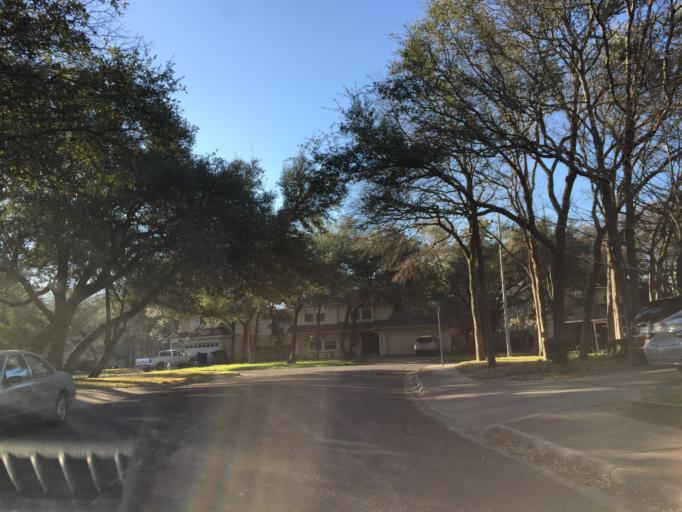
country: US
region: Texas
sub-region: Williamson County
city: Jollyville
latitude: 30.4414
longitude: -97.7683
